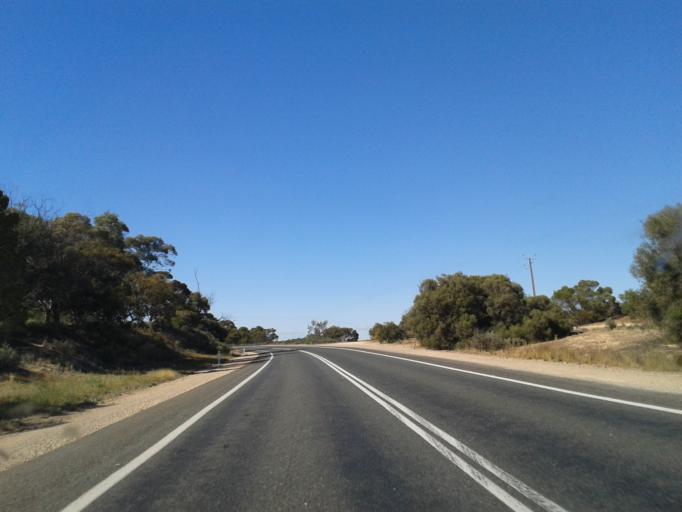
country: AU
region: South Australia
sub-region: Renmark Paringa
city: Renmark
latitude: -34.2369
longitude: 140.8281
